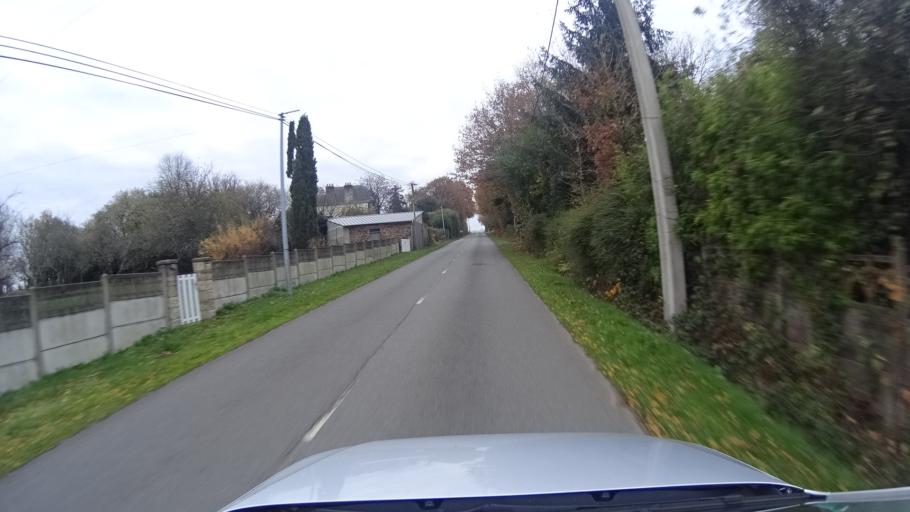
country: FR
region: Pays de la Loire
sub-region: Departement de la Loire-Atlantique
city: Avessac
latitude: 47.6720
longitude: -1.9176
